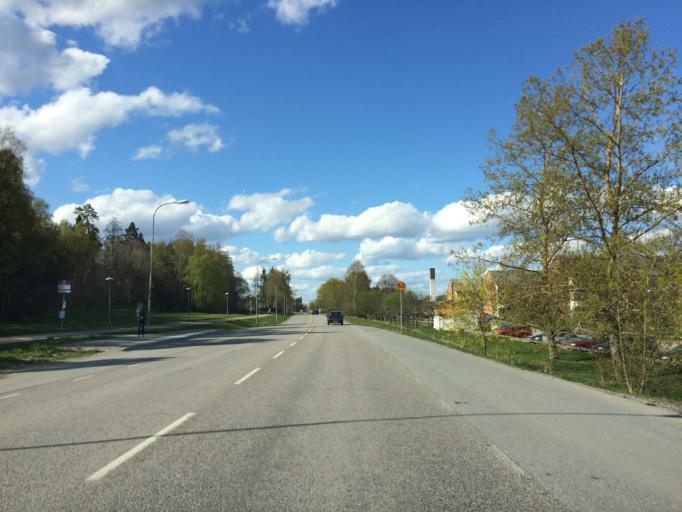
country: SE
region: Stockholm
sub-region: Sollentuna Kommun
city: Sollentuna
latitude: 59.4438
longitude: 17.9263
